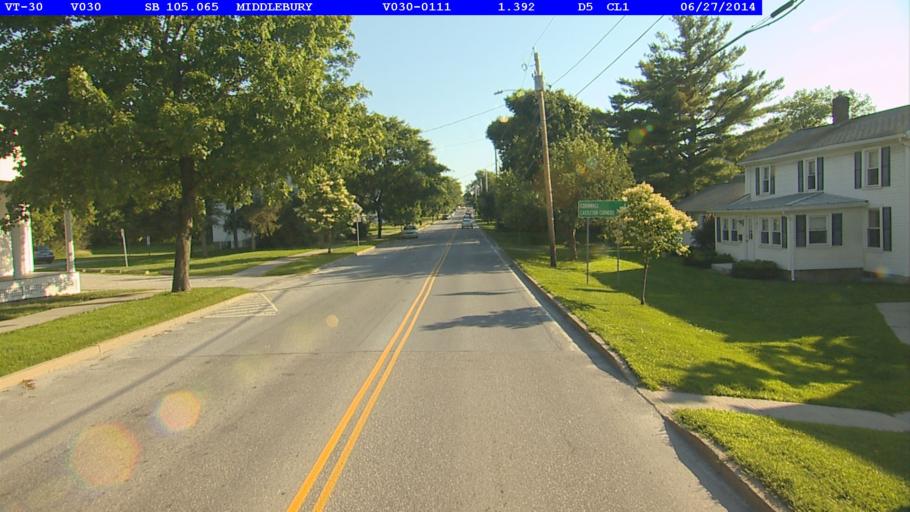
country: US
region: Vermont
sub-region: Addison County
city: Middlebury (village)
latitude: 44.0104
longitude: -73.1714
